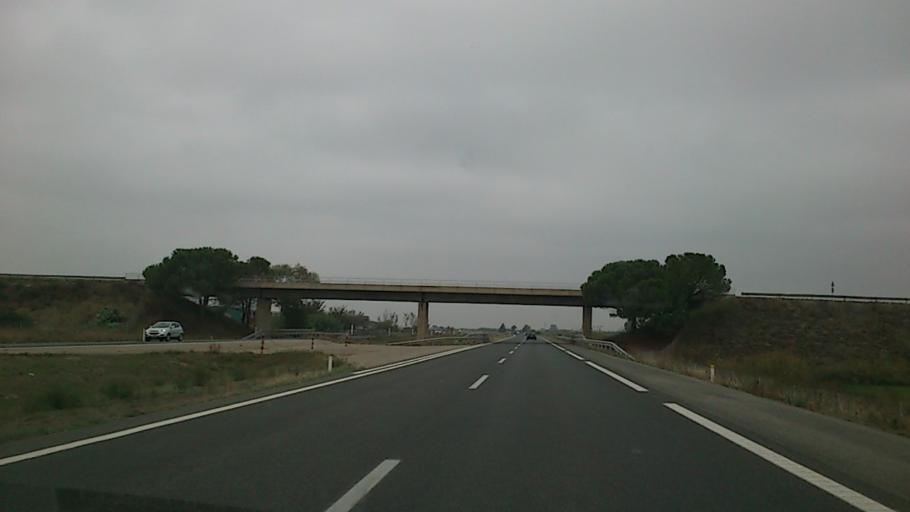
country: ES
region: Aragon
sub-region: Provincia de Zaragoza
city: Torres de Berrellen
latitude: 41.7472
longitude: -1.0627
